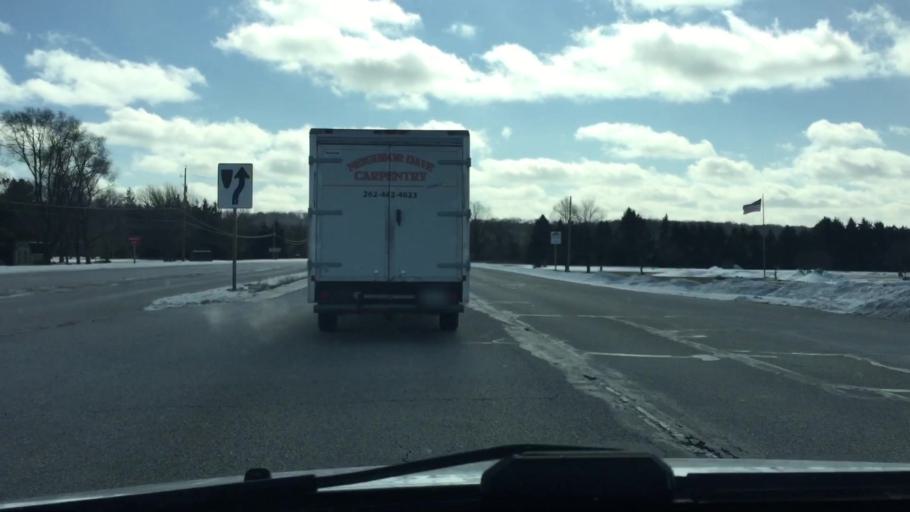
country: US
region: Wisconsin
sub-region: Waukesha County
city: Waukesha
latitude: 42.9484
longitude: -88.2283
